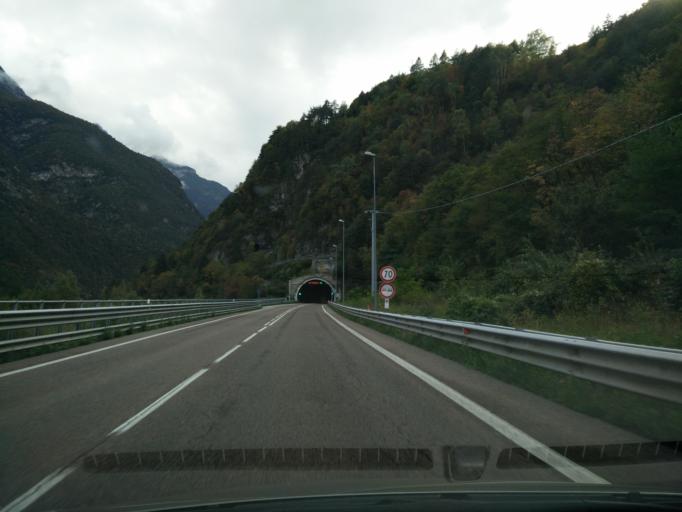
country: IT
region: Veneto
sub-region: Provincia di Belluno
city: Ospitale di Cadore
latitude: 46.3431
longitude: 12.3307
